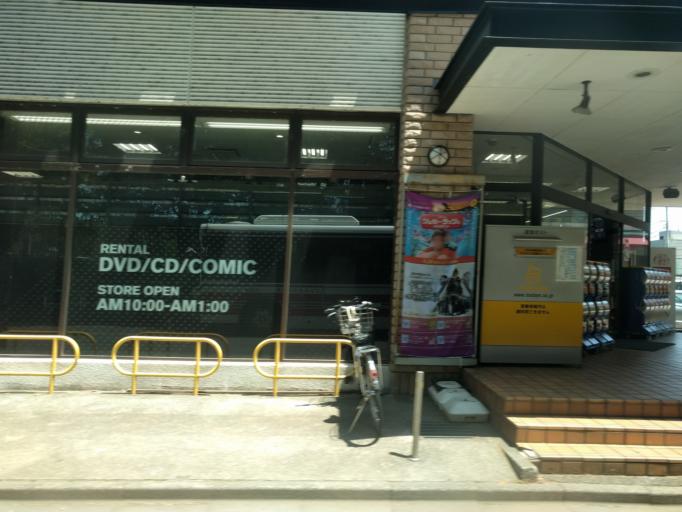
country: JP
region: Tokyo
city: Chofugaoka
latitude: 35.6507
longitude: 139.5967
